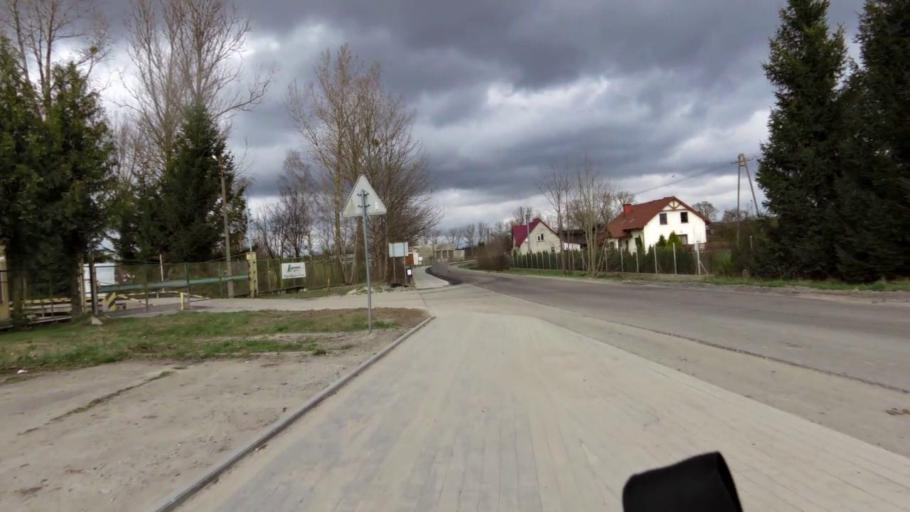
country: PL
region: West Pomeranian Voivodeship
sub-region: Powiat koszalinski
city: Sianow
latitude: 54.2422
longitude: 16.2970
